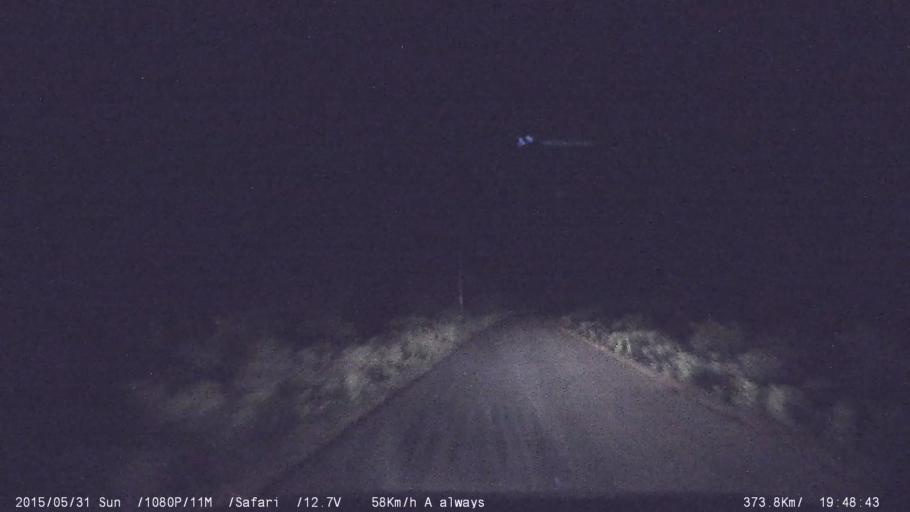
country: IN
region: Karnataka
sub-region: Mandya
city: Malavalli
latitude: 12.3113
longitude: 77.0718
